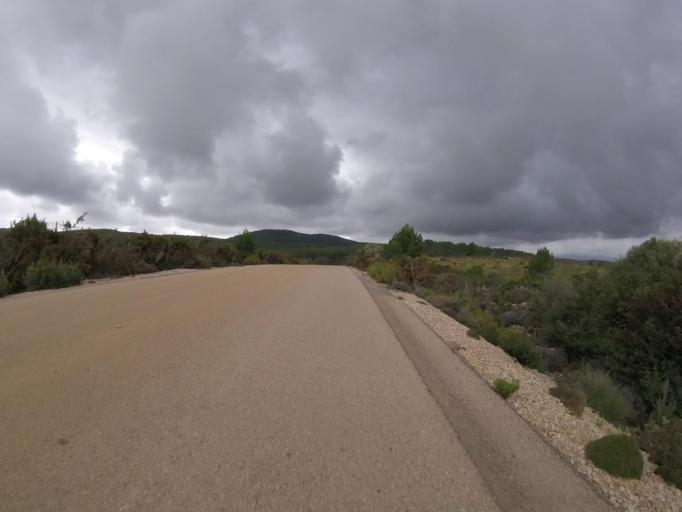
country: ES
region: Valencia
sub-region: Provincia de Castello
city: Benlloch
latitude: 40.2028
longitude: 0.0651
